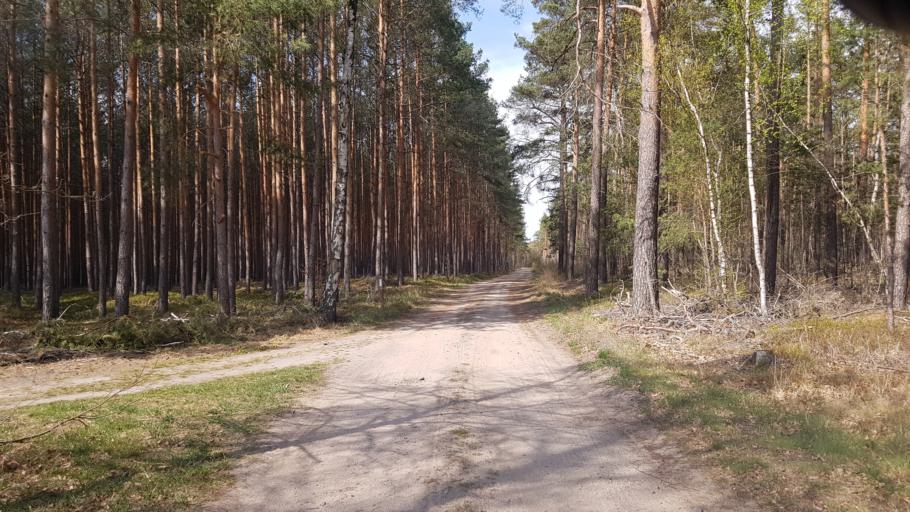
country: DE
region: Brandenburg
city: Ruckersdorf
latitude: 51.5547
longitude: 13.6282
